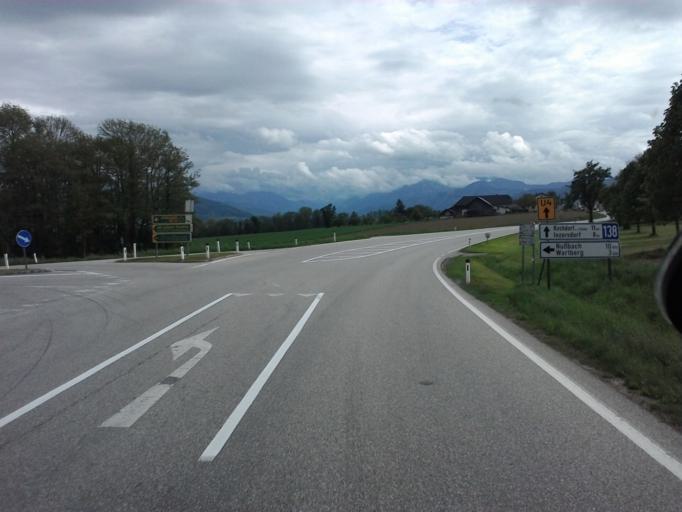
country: AT
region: Upper Austria
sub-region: Politischer Bezirk Kirchdorf an der Krems
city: Kremsmunster
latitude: 47.9820
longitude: 14.0798
